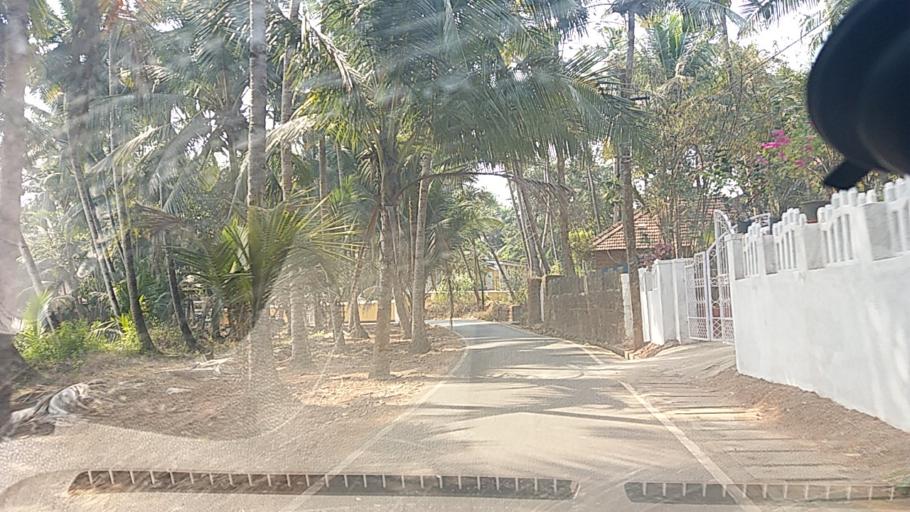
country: IN
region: Goa
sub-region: South Goa
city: Sancoale
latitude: 15.3607
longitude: 73.8878
